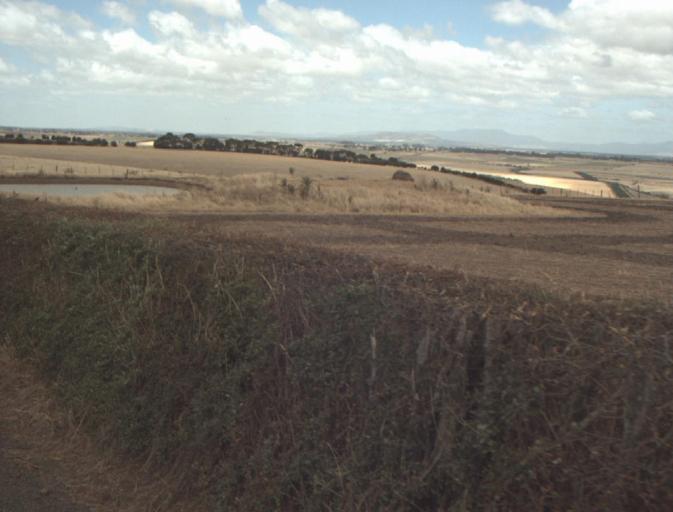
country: AU
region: Tasmania
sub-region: Northern Midlands
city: Evandale
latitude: -41.5228
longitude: 147.2646
